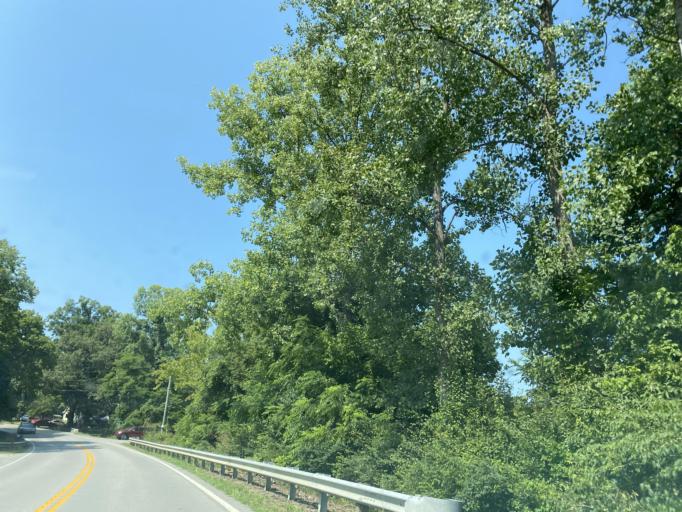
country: US
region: Kentucky
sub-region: Kenton County
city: Ryland Heights
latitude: 38.9255
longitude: -84.4384
